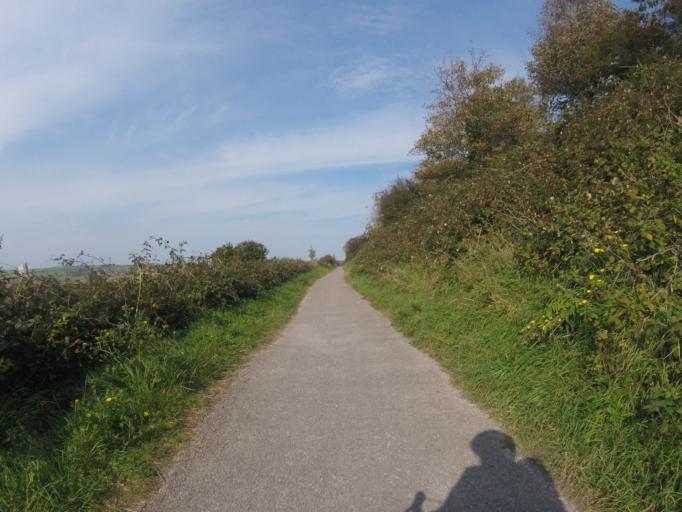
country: GB
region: England
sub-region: East Sussex
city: Portslade
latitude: 50.8636
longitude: -0.2014
